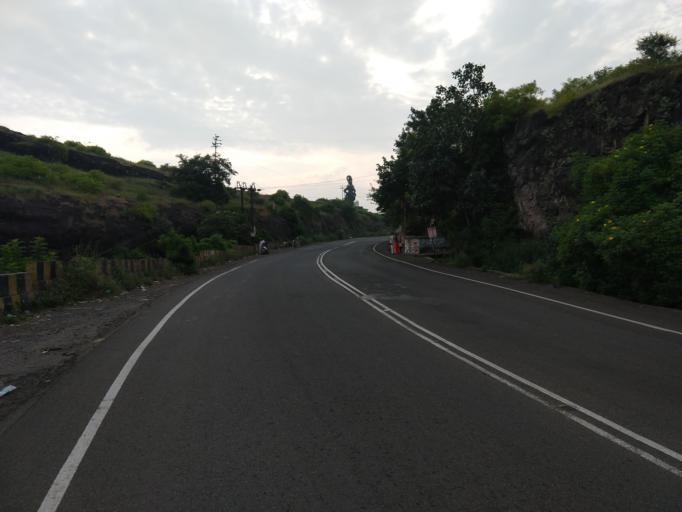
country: IN
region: Maharashtra
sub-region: Pune Division
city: Sasvad
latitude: 18.4160
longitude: 74.0042
